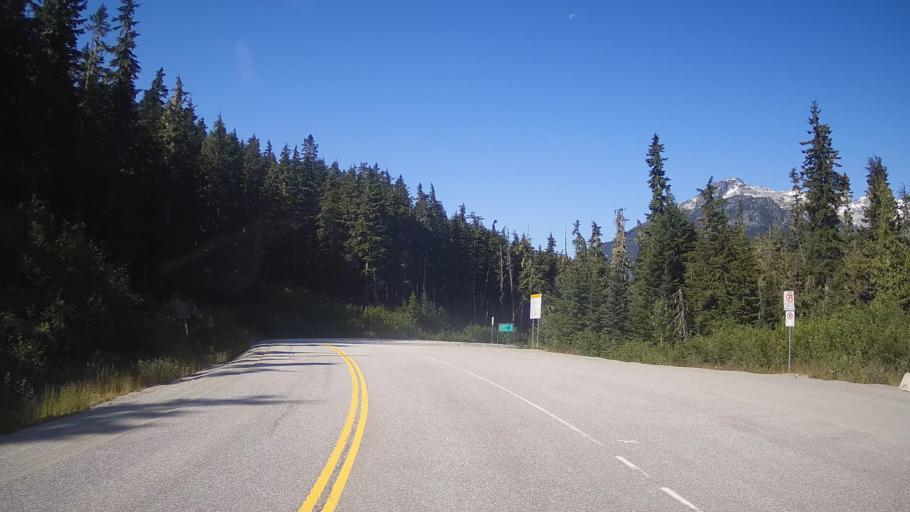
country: CA
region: British Columbia
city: Pemberton
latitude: 50.3675
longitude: -122.5058
